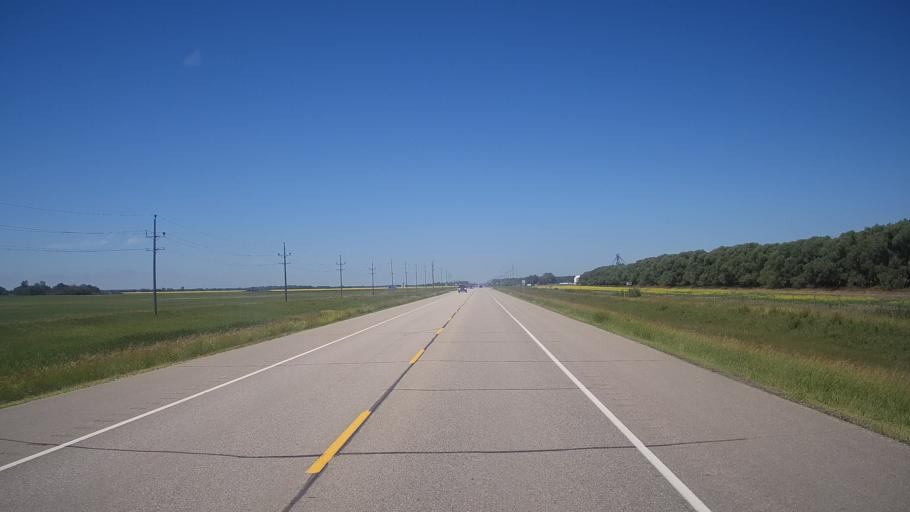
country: CA
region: Manitoba
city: Neepawa
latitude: 50.2257
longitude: -99.0684
